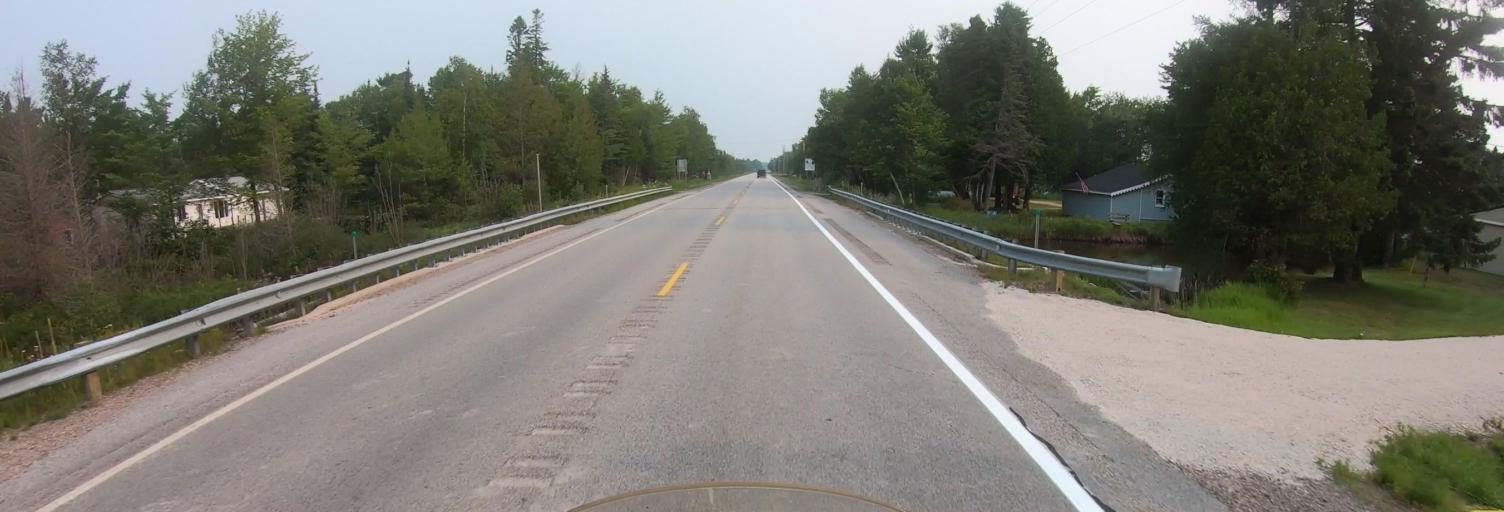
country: US
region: Michigan
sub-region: Luce County
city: Newberry
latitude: 46.5822
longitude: -85.0366
